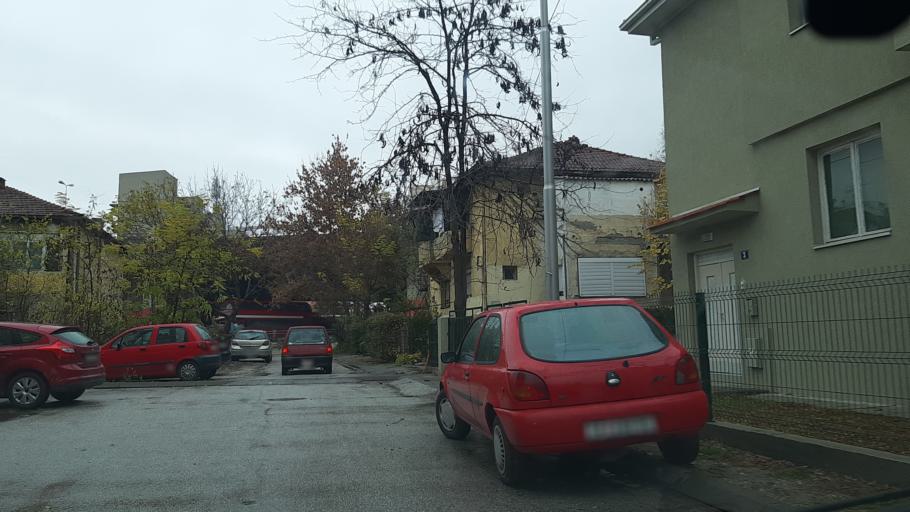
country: MK
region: Karpos
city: Skopje
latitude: 41.9892
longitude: 21.4458
